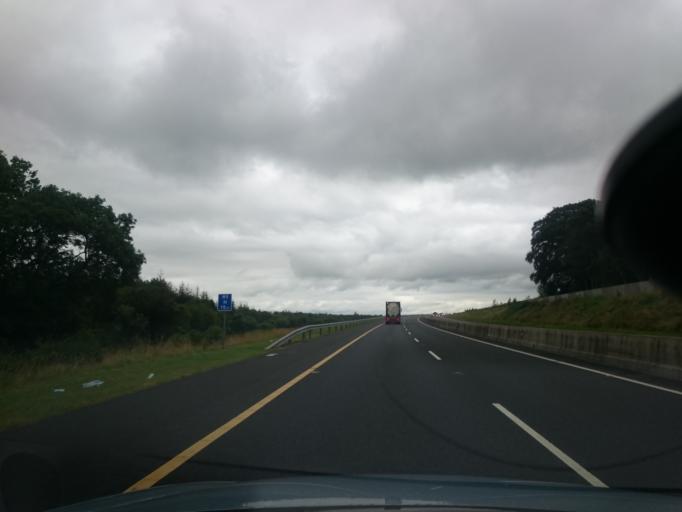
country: IE
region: Leinster
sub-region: Kildare
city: Old Kilcullen
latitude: 53.0511
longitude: -6.7874
